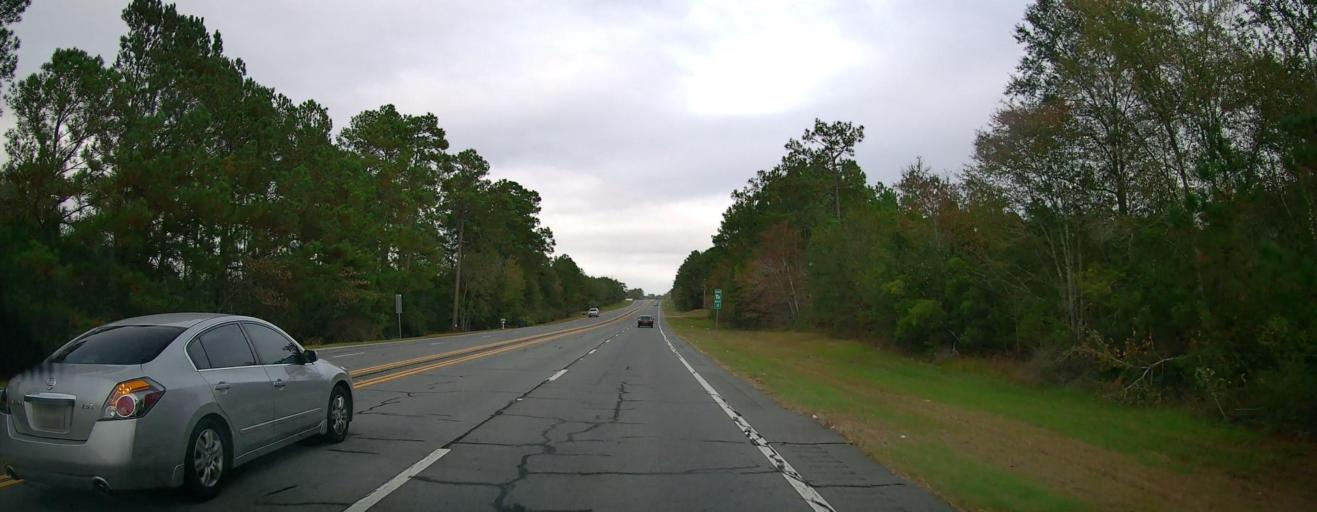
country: US
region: Georgia
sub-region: Colquitt County
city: Moultrie
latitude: 31.2480
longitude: -83.7217
